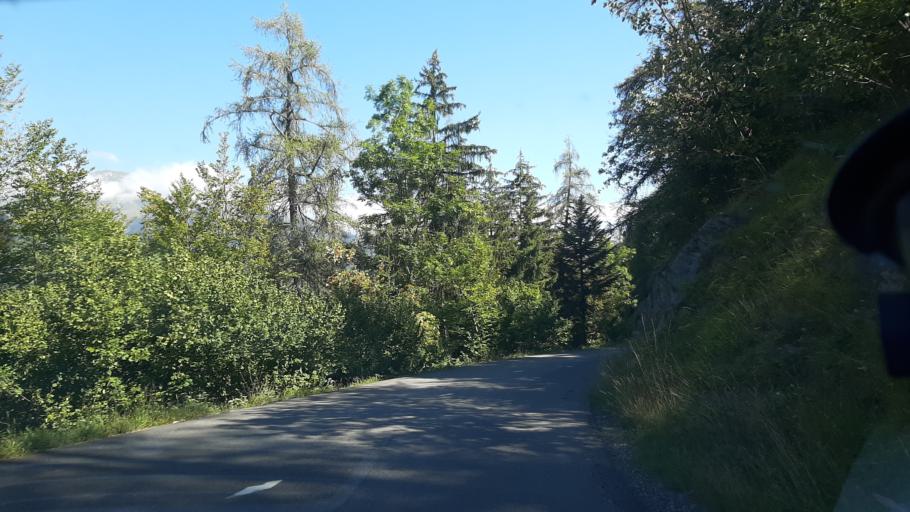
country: FR
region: Rhone-Alpes
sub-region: Departement de la Savoie
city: Aime
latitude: 45.5208
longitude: 6.6008
